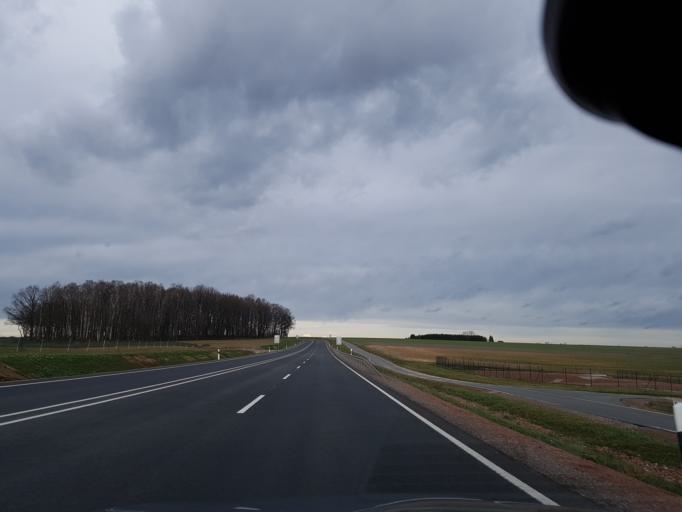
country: DE
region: Saxony
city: Niederstriegis
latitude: 51.0424
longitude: 13.1146
